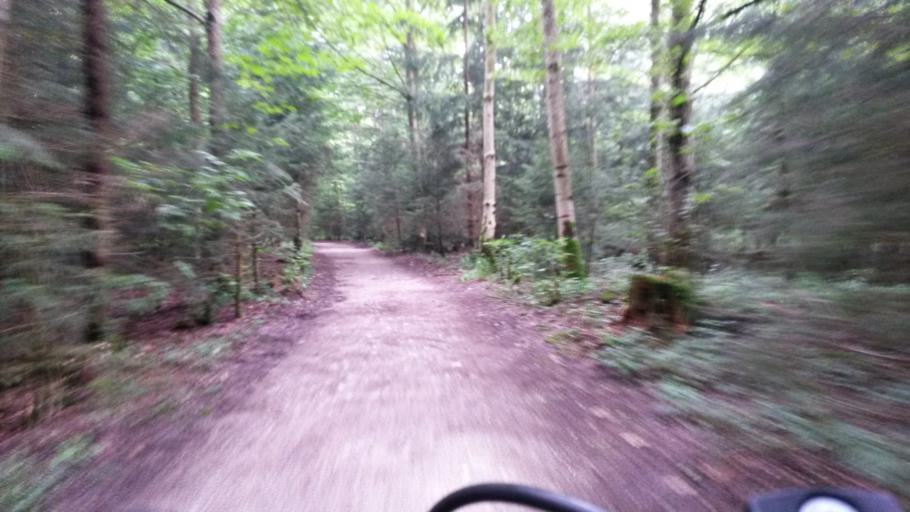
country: DE
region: Bavaria
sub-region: Upper Bavaria
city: Hoslwang
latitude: 47.9223
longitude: 12.3436
